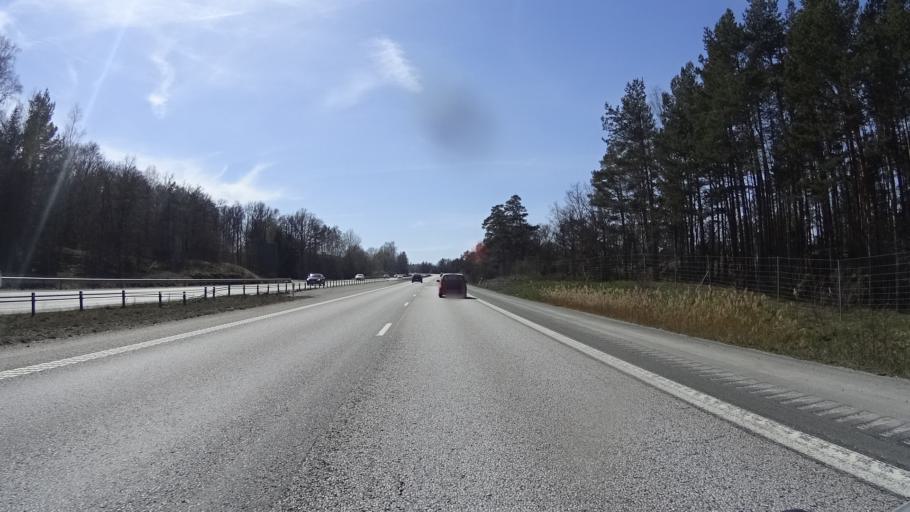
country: SE
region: Joenkoeping
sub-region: Jonkopings Kommun
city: Graenna
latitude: 57.9834
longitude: 14.4036
